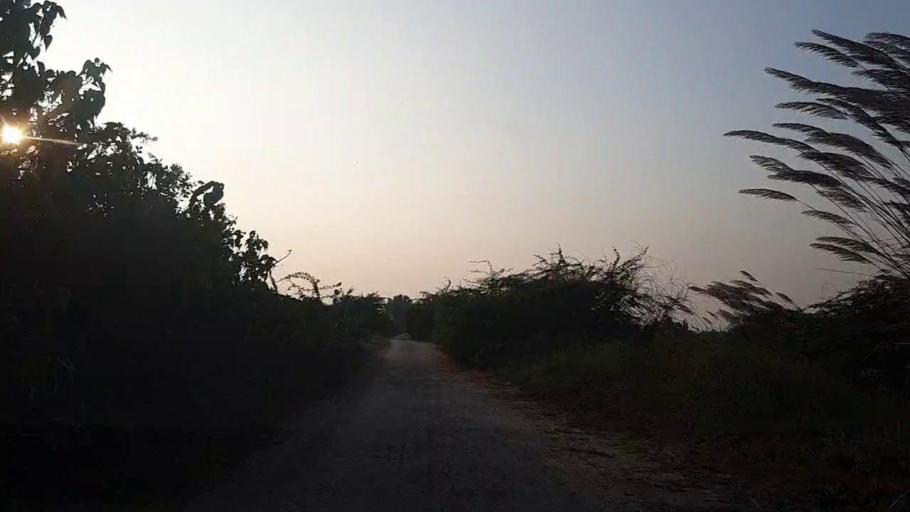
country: PK
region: Sindh
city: Mirpur Sakro
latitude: 24.5585
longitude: 67.5916
